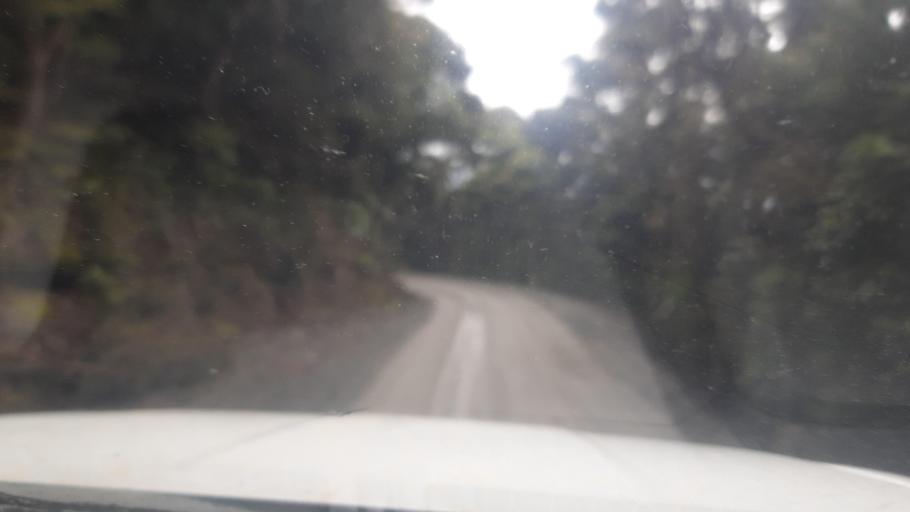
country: NZ
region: Northland
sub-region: Far North District
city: Taipa
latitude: -35.0682
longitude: 173.5261
